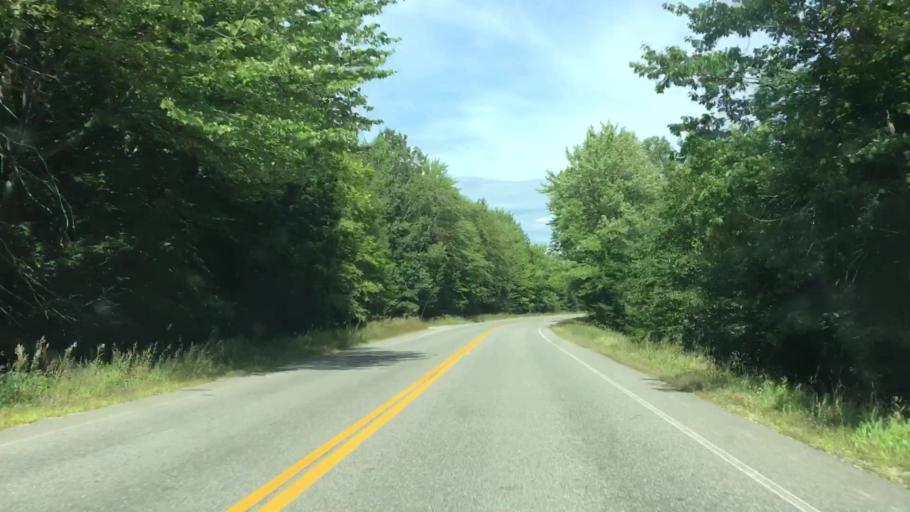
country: US
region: Maine
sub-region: Penobscot County
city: Lincoln
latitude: 45.3787
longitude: -68.5491
